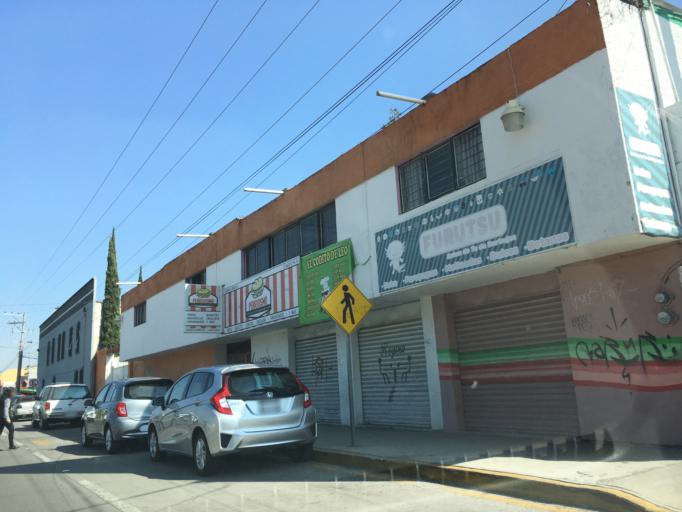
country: MX
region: Michoacan
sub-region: Morelia
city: Morelos
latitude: 19.6830
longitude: -101.2257
